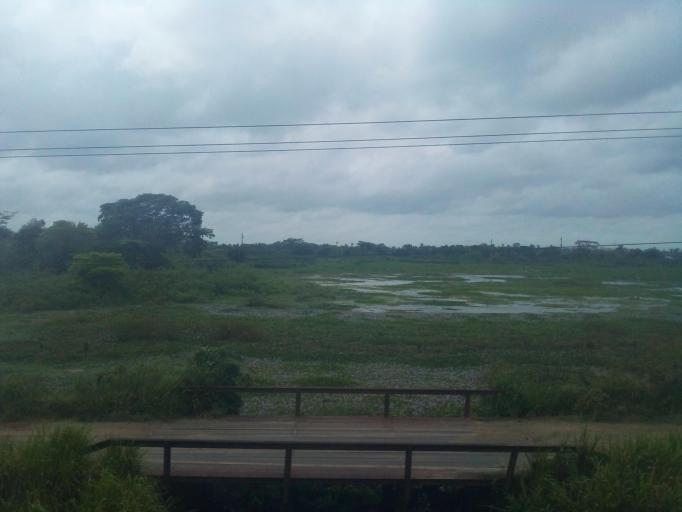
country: BR
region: Maranhao
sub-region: Arari
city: Arari
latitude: -3.5684
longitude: -44.6840
